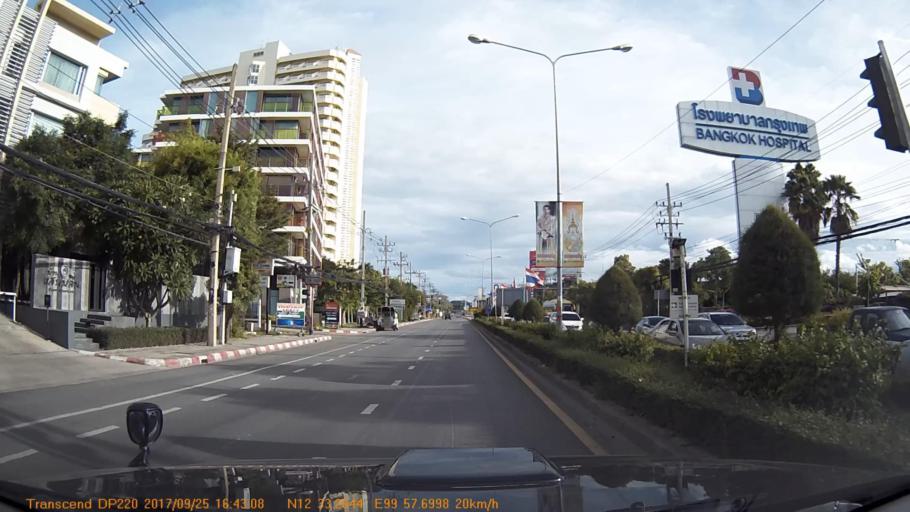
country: TH
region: Prachuap Khiri Khan
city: Hua Hin
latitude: 12.5550
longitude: 99.9616
